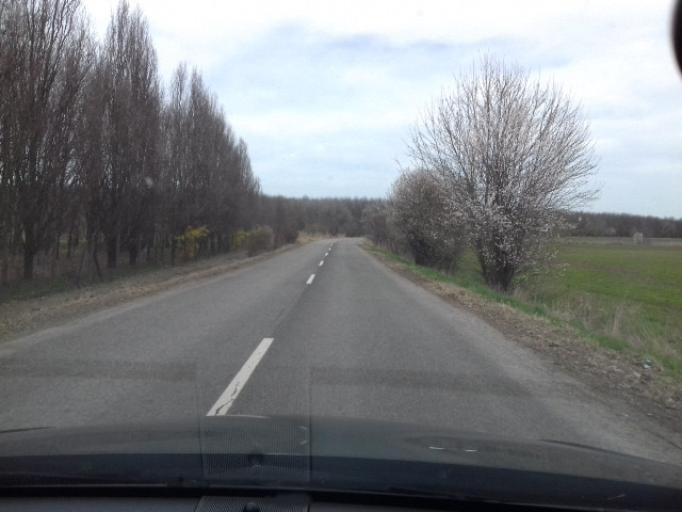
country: HU
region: Bacs-Kiskun
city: Tiszakecske
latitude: 46.8887
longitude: 20.1275
